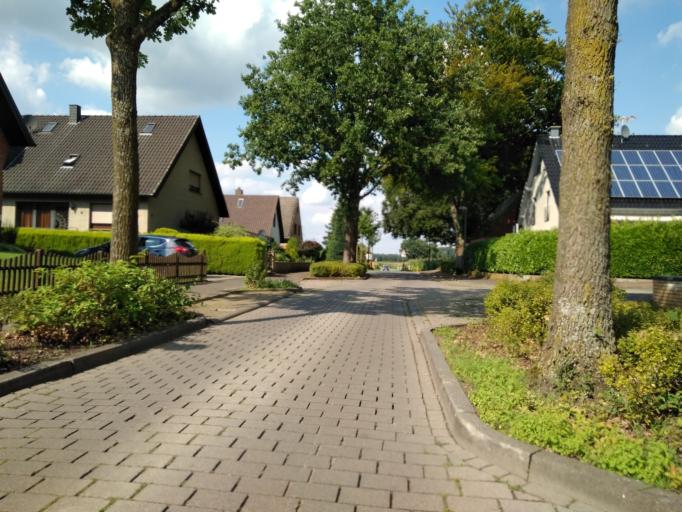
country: DE
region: North Rhine-Westphalia
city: Dorsten
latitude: 51.7219
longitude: 6.9701
